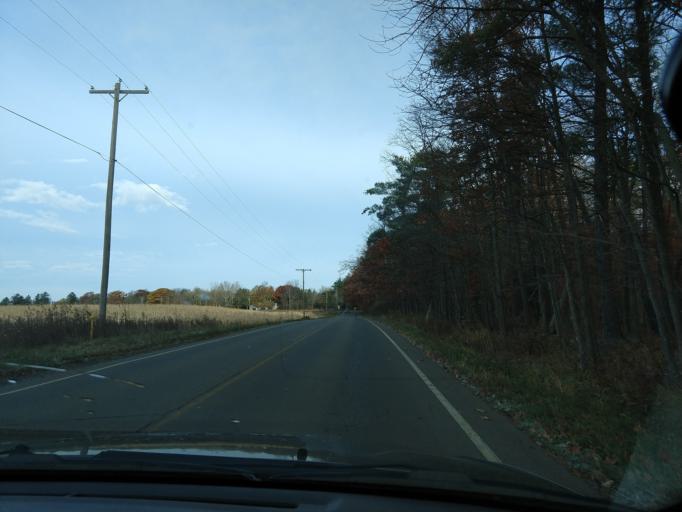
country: US
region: New York
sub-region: Tompkins County
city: Northeast Ithaca
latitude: 42.4657
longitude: -76.4466
